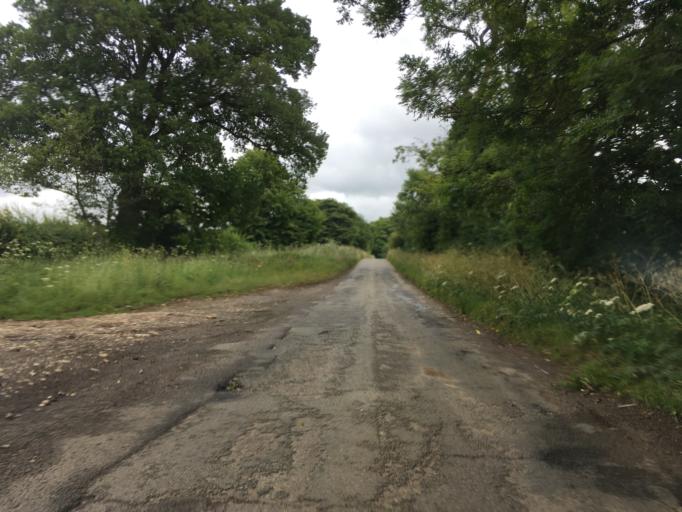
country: GB
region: England
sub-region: Gloucestershire
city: Mickleton
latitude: 52.0665
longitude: -1.7714
